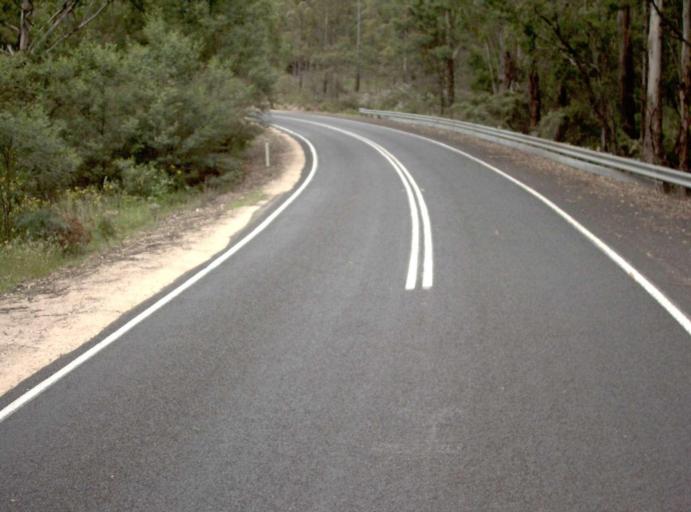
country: AU
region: New South Wales
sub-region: Bombala
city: Bombala
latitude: -37.4076
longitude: 149.1990
